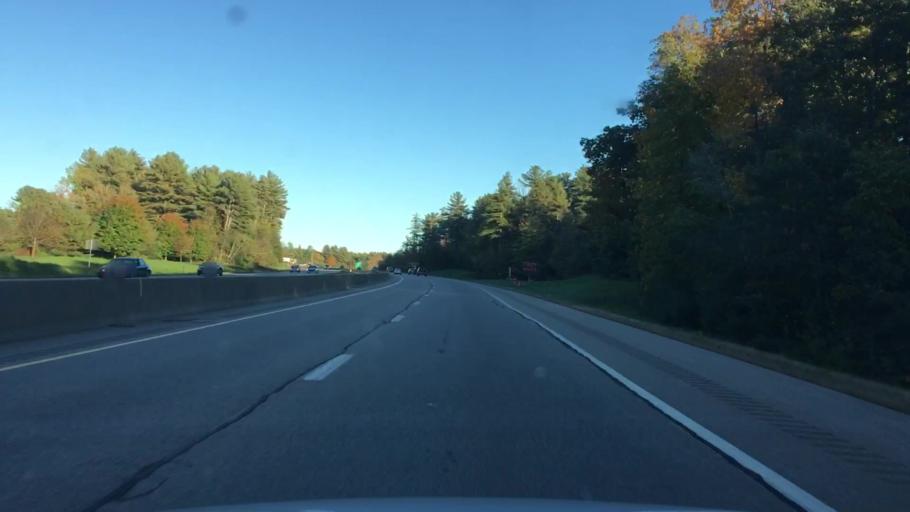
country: US
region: New Hampshire
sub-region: Rockingham County
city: Exeter
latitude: 43.0075
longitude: -70.9987
